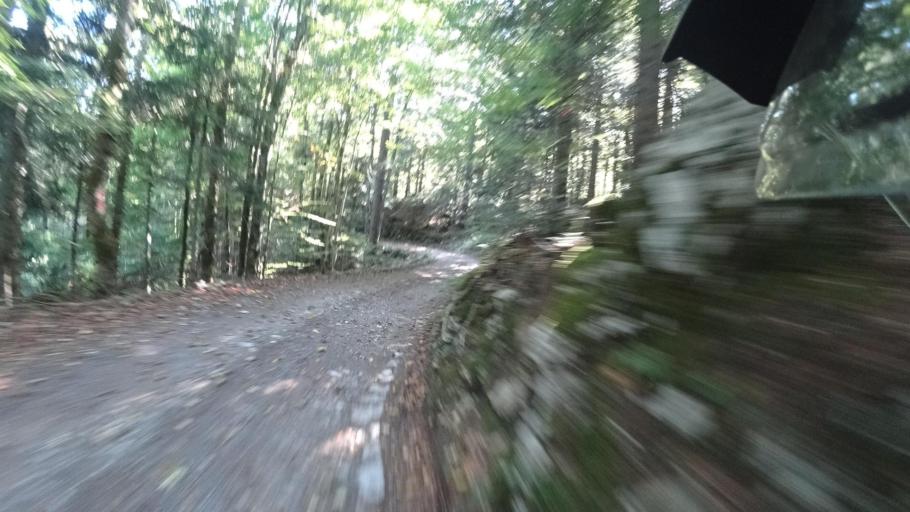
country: HR
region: Primorsko-Goranska
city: Vrbovsko
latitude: 45.2599
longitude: 15.1094
